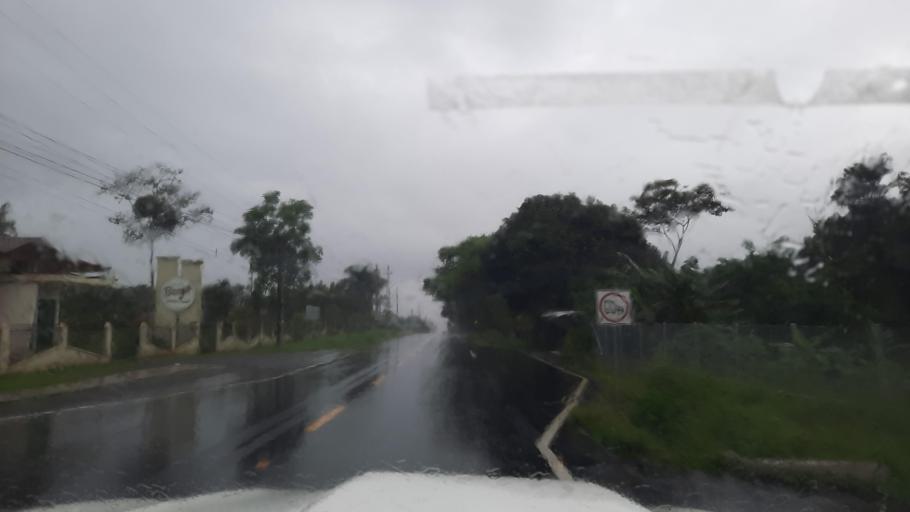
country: PA
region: Chiriqui
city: Sortova
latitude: 8.5859
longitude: -82.6371
